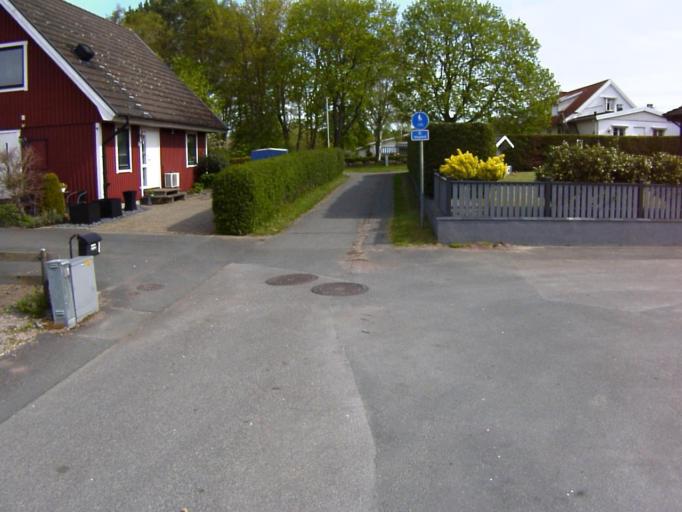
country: SE
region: Skane
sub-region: Kristianstads Kommun
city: Fjalkinge
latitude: 56.0380
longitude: 14.2743
